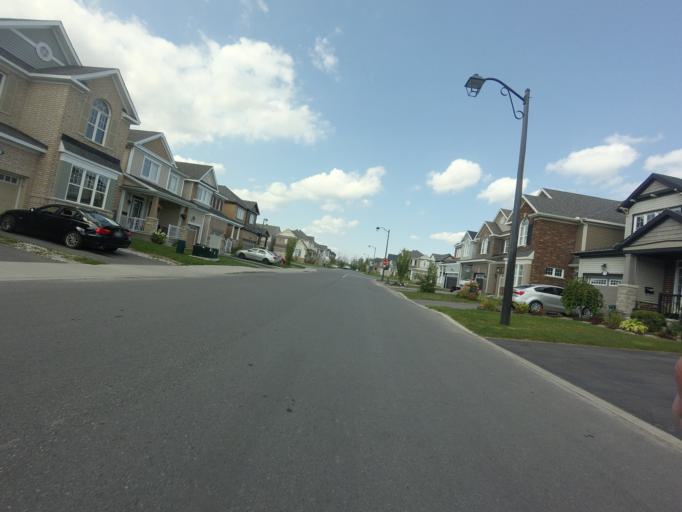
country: CA
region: Ontario
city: Bells Corners
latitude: 45.2452
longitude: -75.7336
